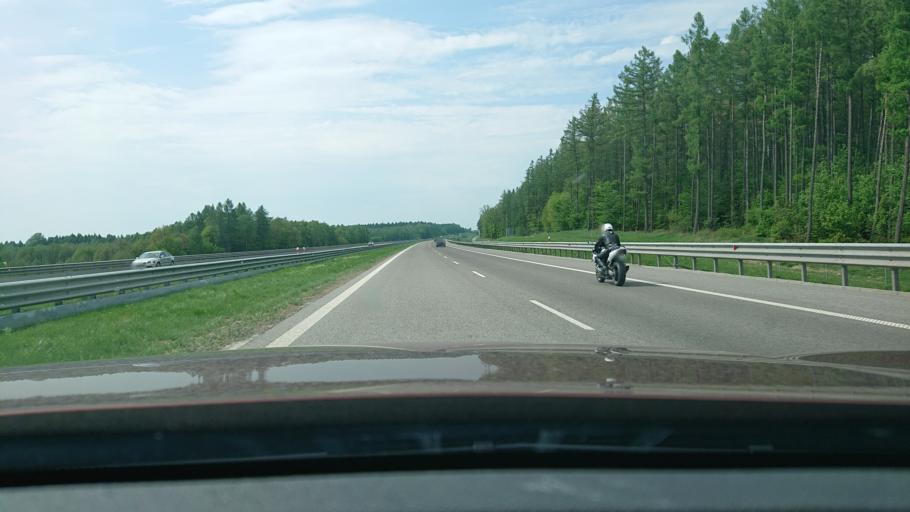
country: PL
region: Subcarpathian Voivodeship
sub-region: Powiat jaroslawski
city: Pawlosiow
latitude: 49.9860
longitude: 22.6173
